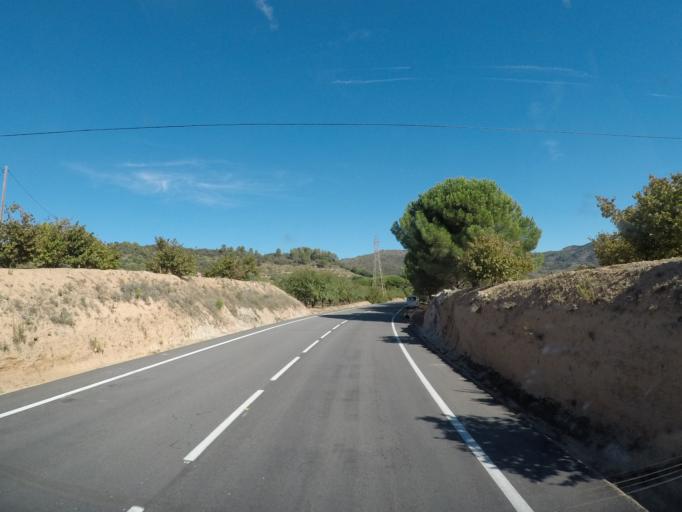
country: ES
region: Catalonia
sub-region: Provincia de Tarragona
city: Falset
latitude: 41.1590
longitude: 0.8145
